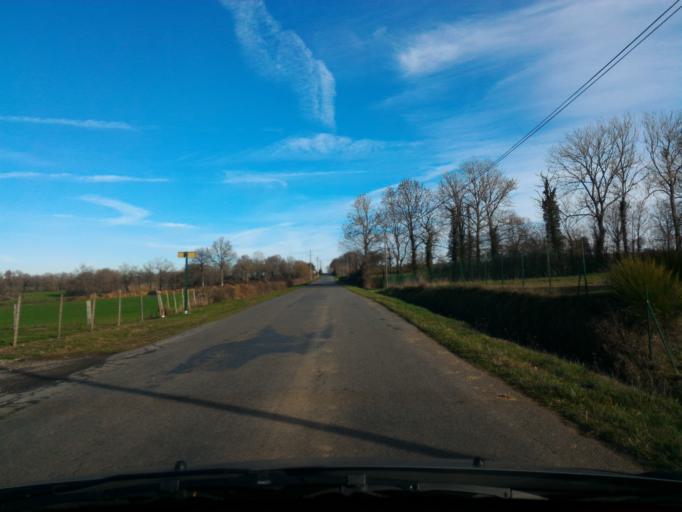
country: FR
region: Poitou-Charentes
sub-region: Departement de la Charente
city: Etagnac
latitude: 45.9255
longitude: 0.7573
